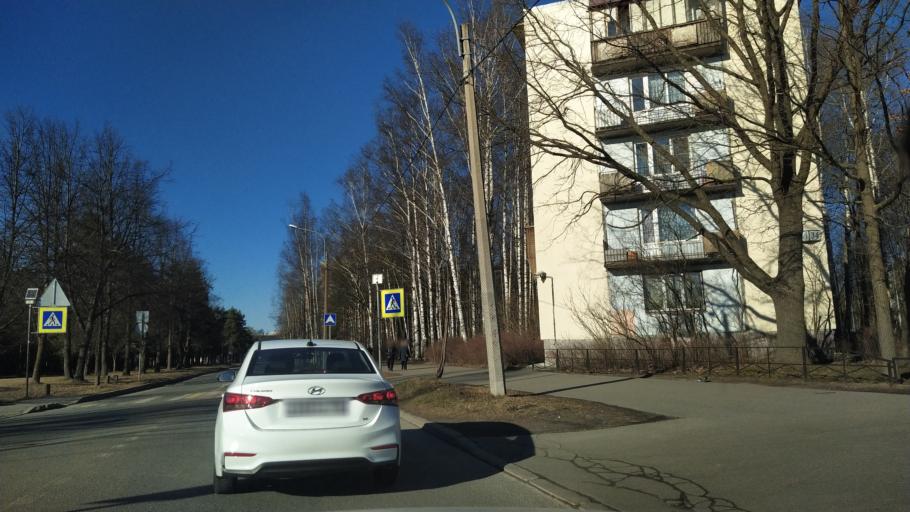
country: RU
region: Leningrad
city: Akademicheskoe
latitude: 60.0016
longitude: 30.4220
